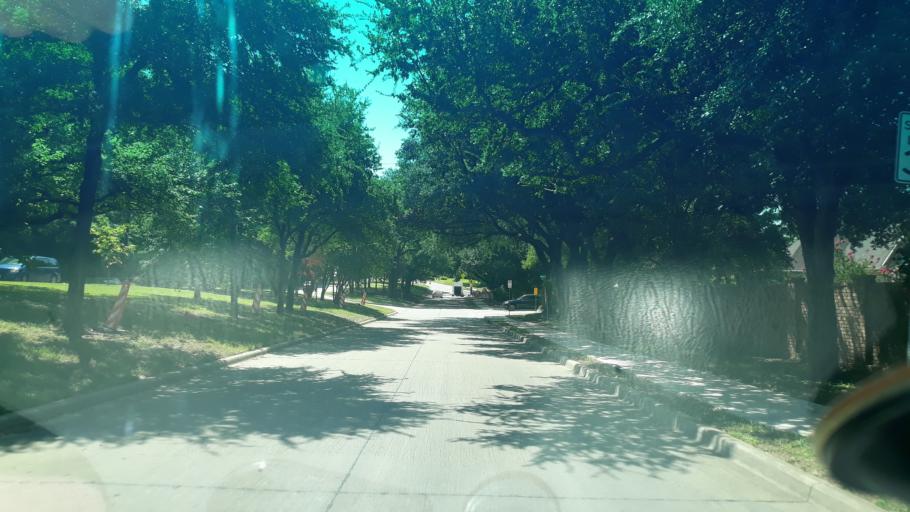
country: US
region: Texas
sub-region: Dallas County
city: Highland Park
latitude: 32.8135
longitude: -96.7236
